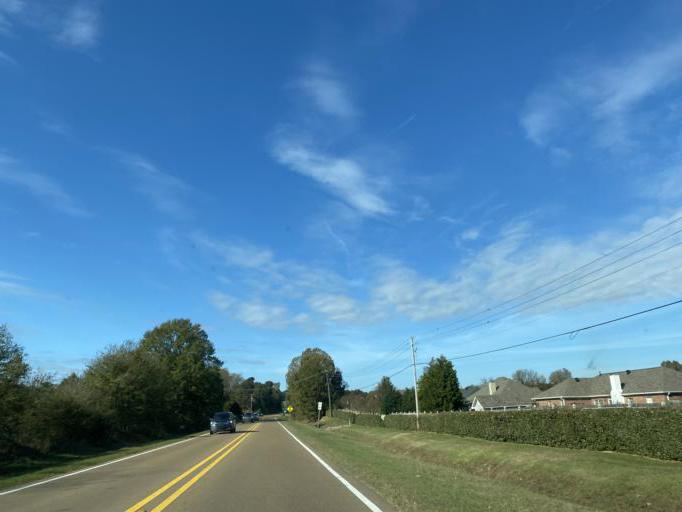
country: US
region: Mississippi
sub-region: Madison County
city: Madison
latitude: 32.4804
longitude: -90.1622
